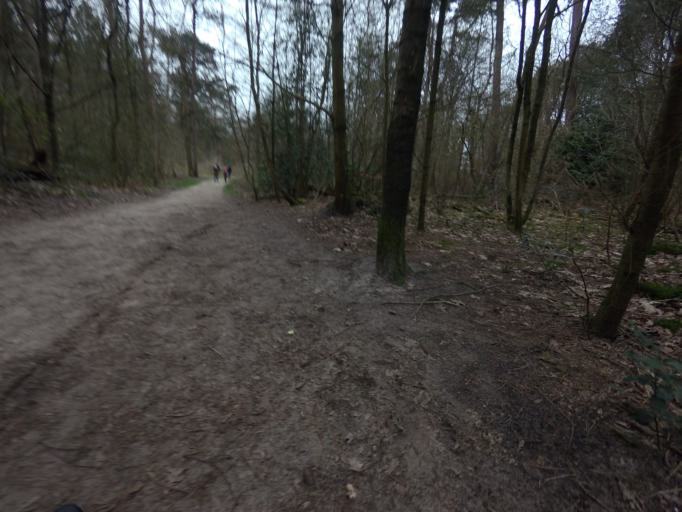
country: NL
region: Utrecht
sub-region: Gemeente Utrechtse Heuvelrug
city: Doorn
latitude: 52.0406
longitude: 5.3509
